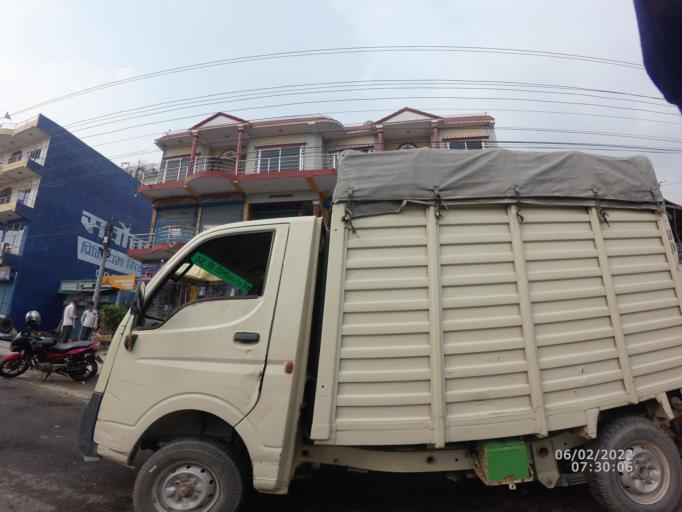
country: NP
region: Western Region
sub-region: Lumbini Zone
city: Bhairahawa
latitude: 27.5177
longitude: 83.4519
